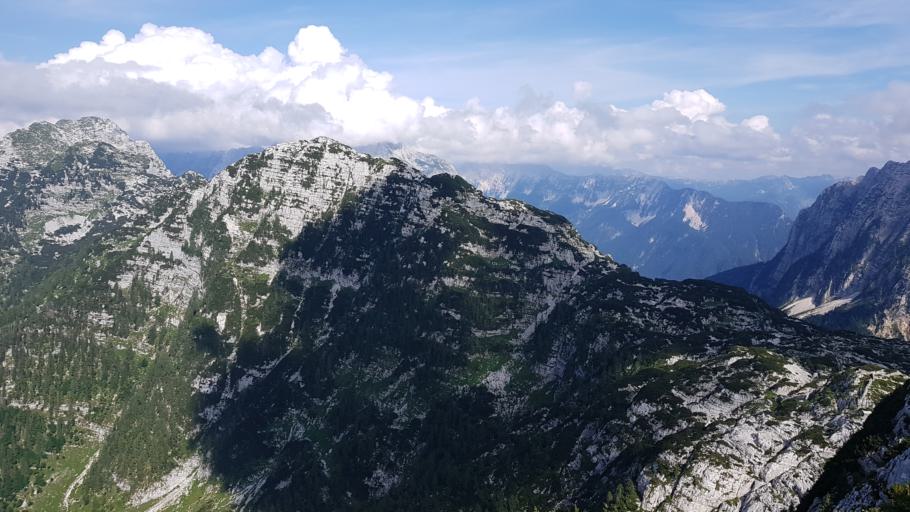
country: SI
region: Bovec
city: Bovec
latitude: 46.3896
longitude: 13.5257
